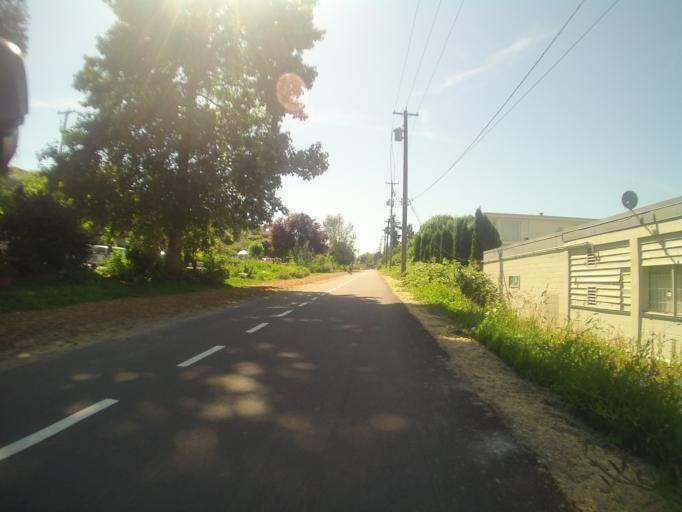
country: CA
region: British Columbia
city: West End
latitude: 49.2665
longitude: -123.1460
